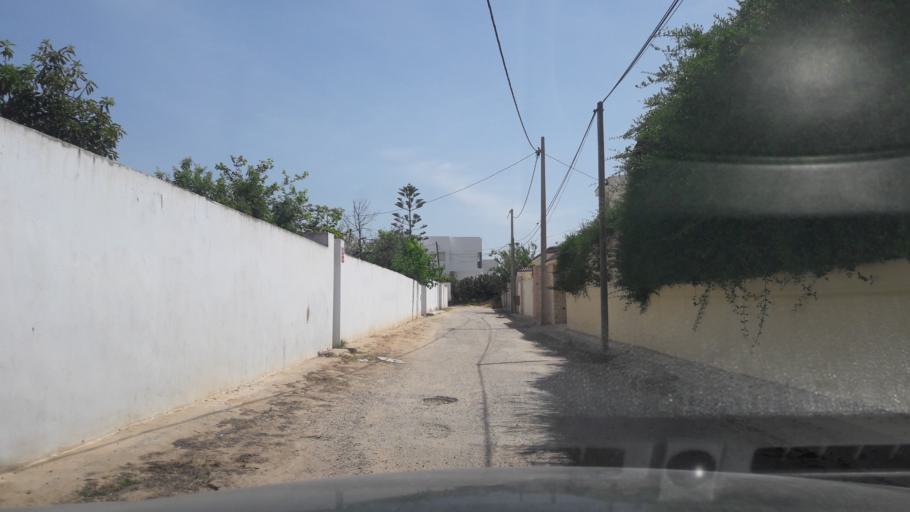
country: TN
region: Safaqis
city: Al Qarmadah
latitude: 34.7883
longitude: 10.7568
